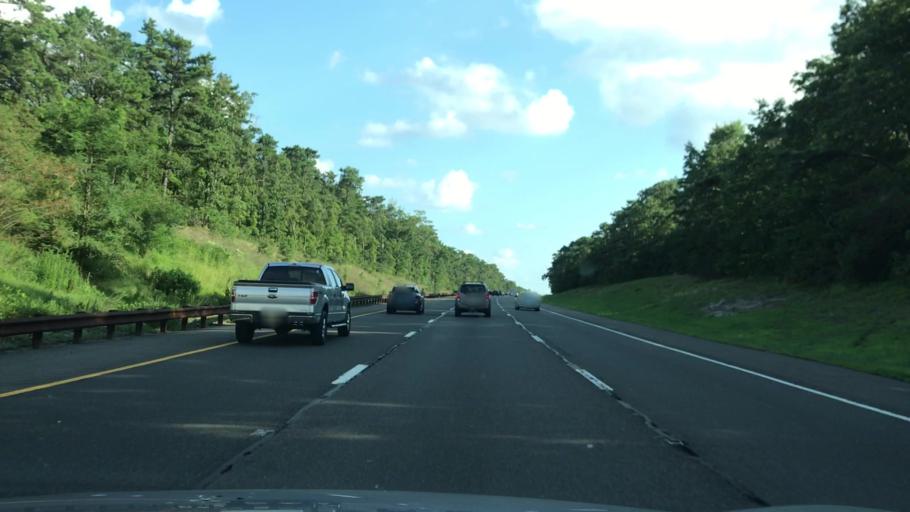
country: US
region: New Jersey
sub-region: Ocean County
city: South Toms River
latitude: 39.9331
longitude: -74.2091
